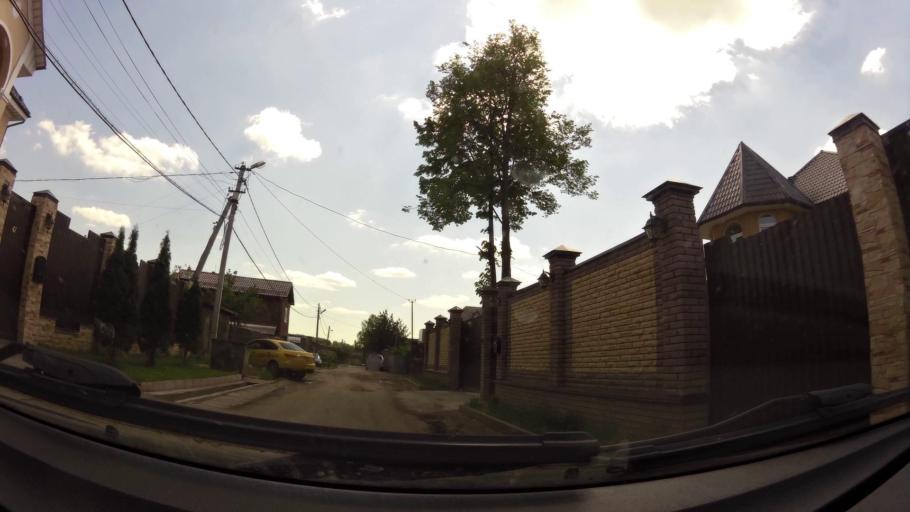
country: RU
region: Moscow
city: Lianozovo
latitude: 55.9266
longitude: 37.6146
